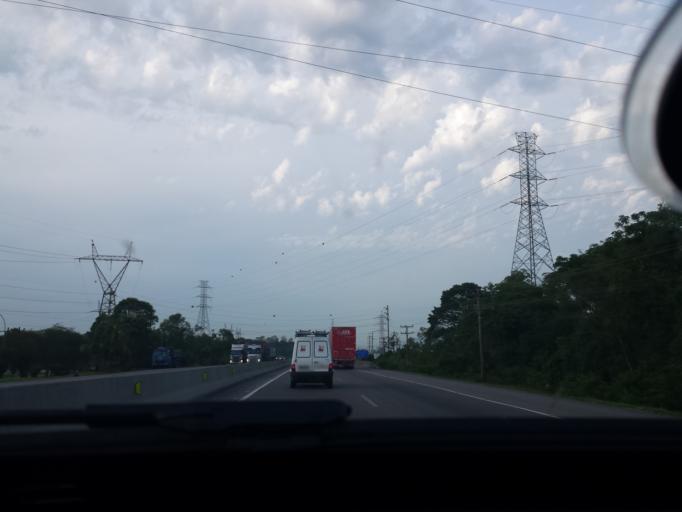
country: BR
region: Santa Catarina
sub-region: Tubarao
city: Tubarao
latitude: -28.4494
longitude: -48.9707
